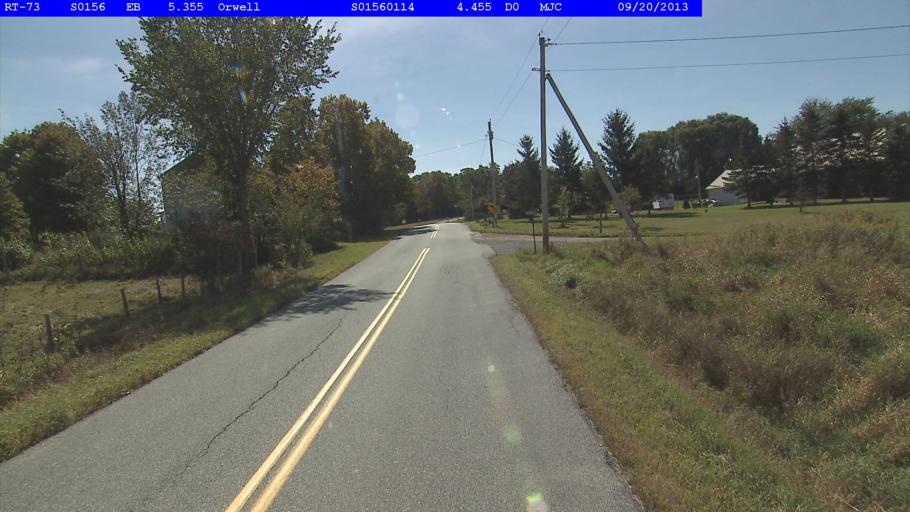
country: US
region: New York
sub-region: Essex County
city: Ticonderoga
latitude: 43.8063
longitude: -73.3123
